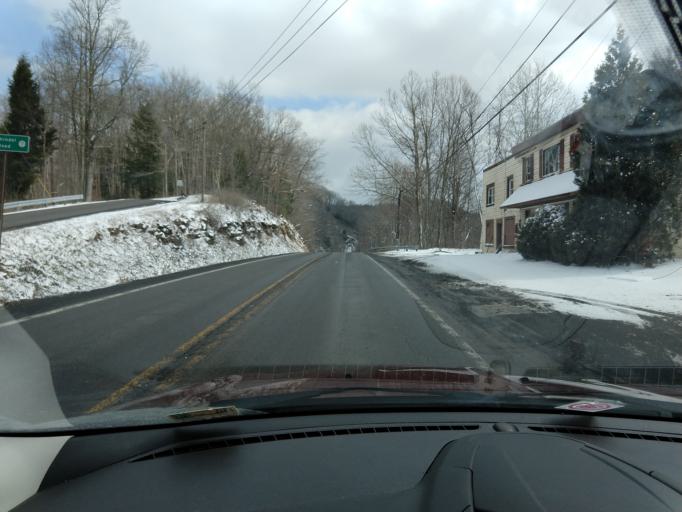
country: US
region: West Virginia
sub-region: Nicholas County
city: Craigsville
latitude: 38.3038
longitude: -80.6483
